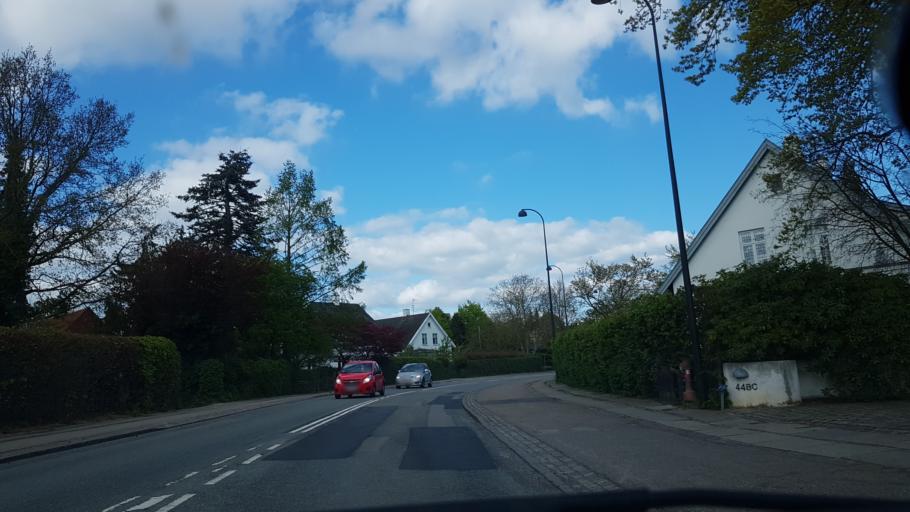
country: DK
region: Capital Region
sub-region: Rudersdal Kommune
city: Holte
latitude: 55.8154
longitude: 12.4819
